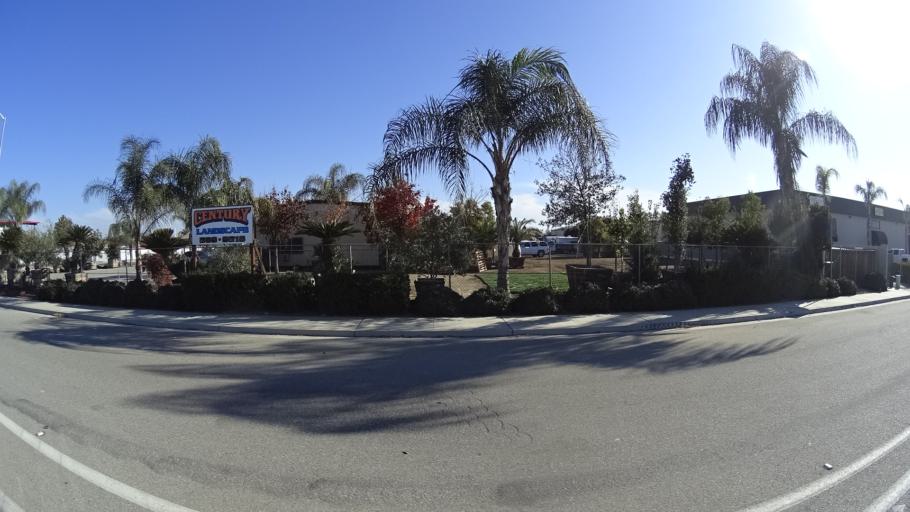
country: US
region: California
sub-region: Kern County
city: Rosedale
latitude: 35.3902
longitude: -119.1455
